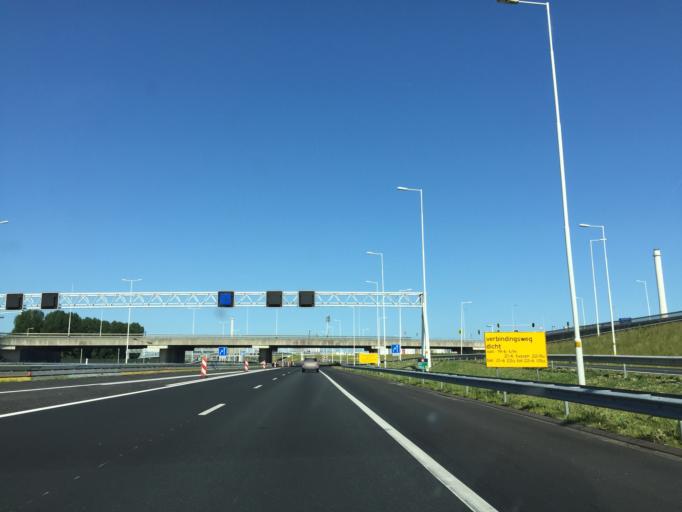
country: NL
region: South Holland
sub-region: Gemeente Schiedam
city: Schiedam
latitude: 51.8749
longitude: 4.3773
